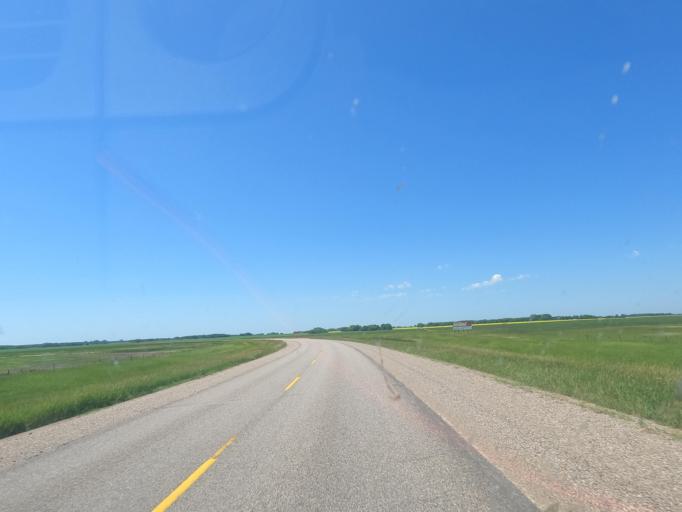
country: CA
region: Manitoba
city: Souris
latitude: 49.6212
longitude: -100.5156
